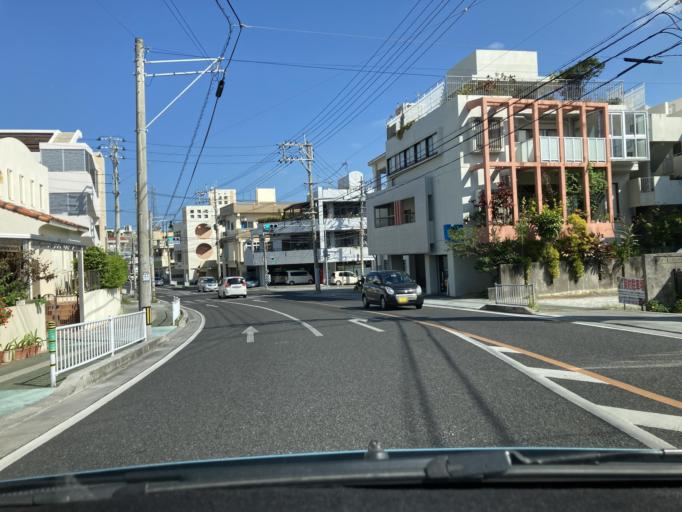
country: JP
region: Okinawa
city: Tomigusuku
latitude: 26.1911
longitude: 127.6707
